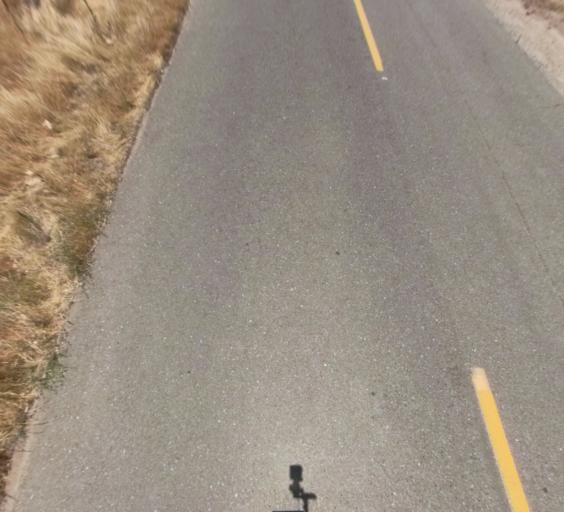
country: US
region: California
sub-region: Madera County
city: Madera Acres
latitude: 37.0457
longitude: -119.9958
